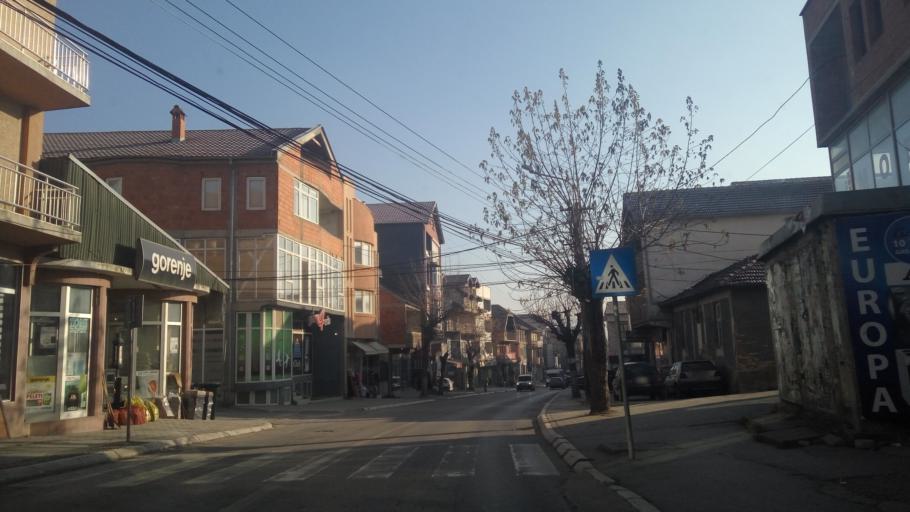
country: XK
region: Gjilan
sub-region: Komuna e Gjilanit
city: Gjilan
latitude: 42.4636
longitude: 21.4644
